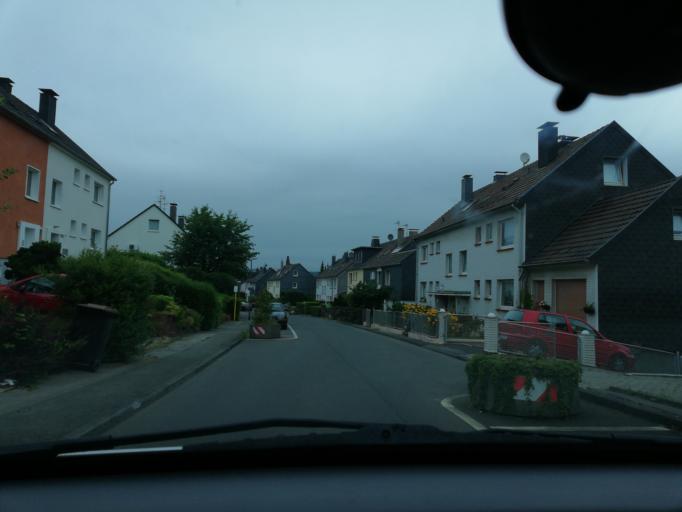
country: DE
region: North Rhine-Westphalia
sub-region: Regierungsbezirk Dusseldorf
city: Wuppertal
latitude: 51.2655
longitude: 7.2319
